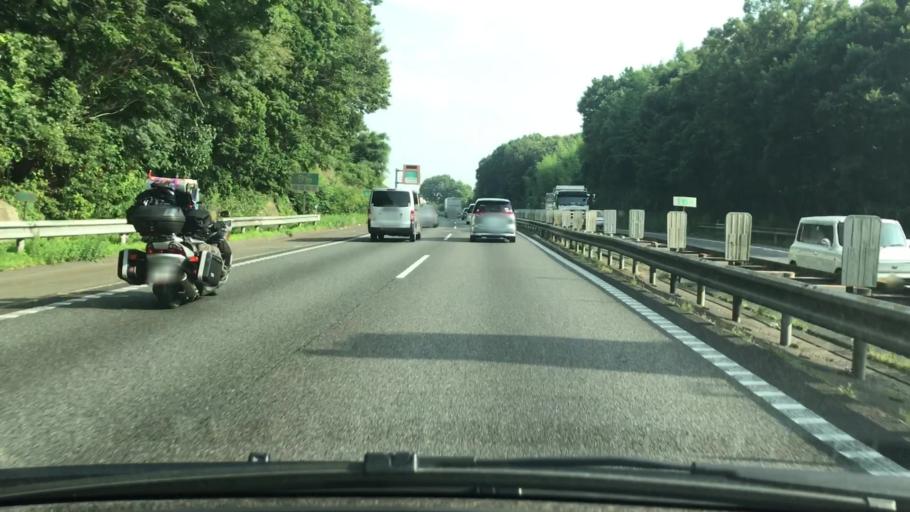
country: JP
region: Hyogo
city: Akashi
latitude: 34.6945
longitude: 134.9688
